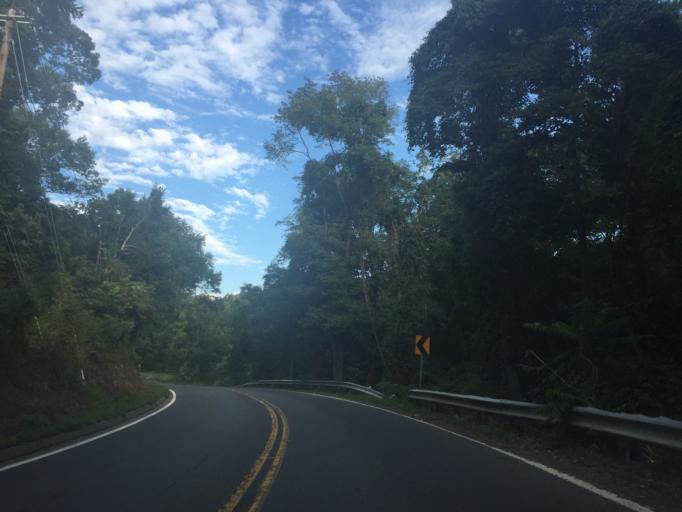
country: US
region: Maryland
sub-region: Montgomery County
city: Montgomery Village
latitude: 39.2051
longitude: -77.1672
